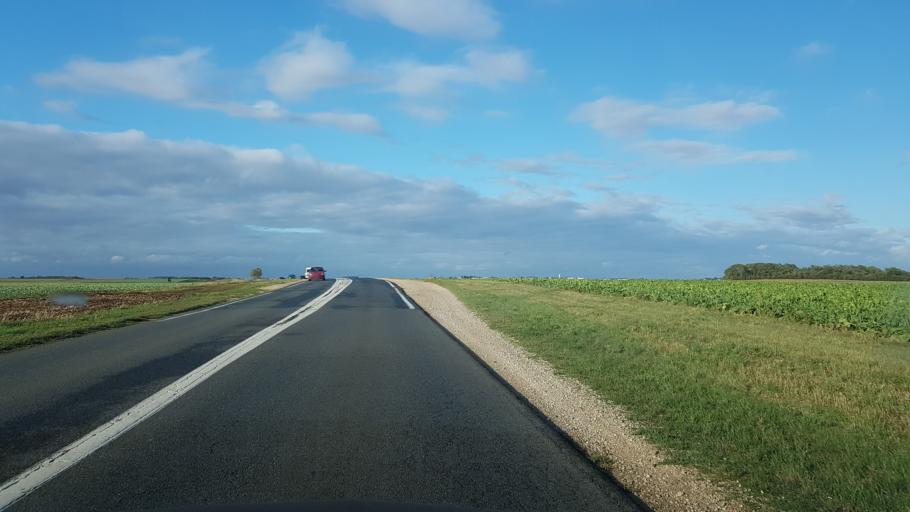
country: FR
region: Centre
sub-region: Departement du Loiret
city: Sermaises
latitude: 48.3015
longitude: 2.2007
